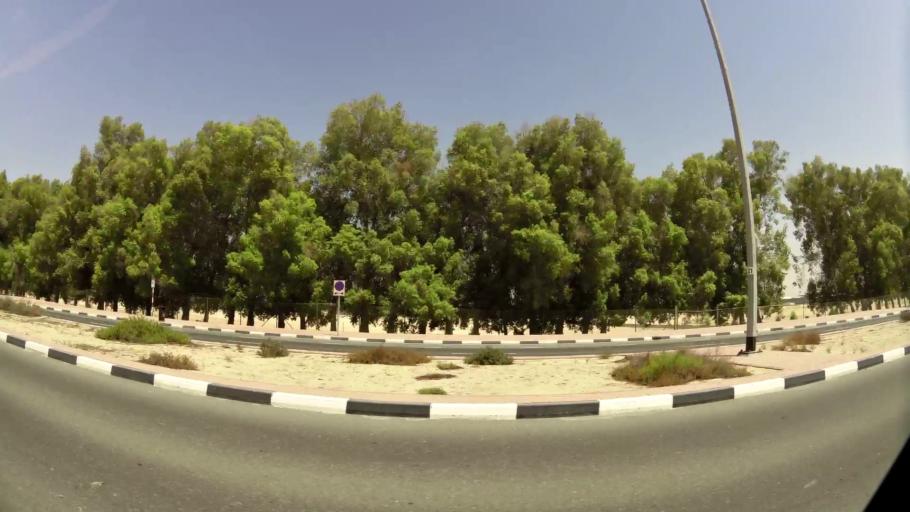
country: AE
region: Dubai
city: Dubai
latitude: 25.1233
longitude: 55.1848
